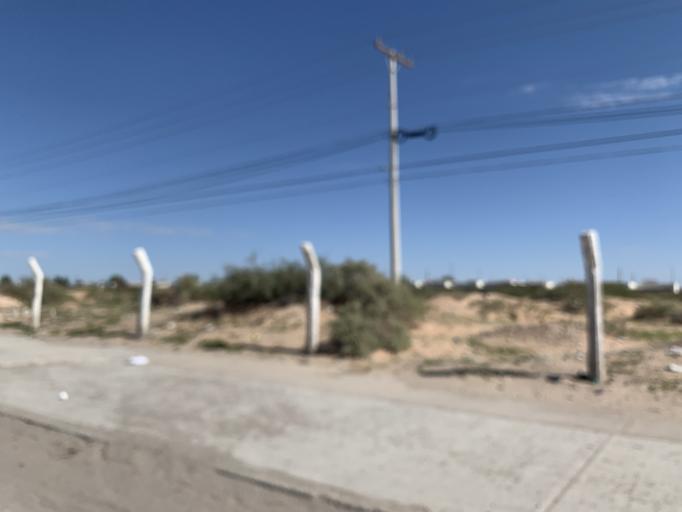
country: US
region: Texas
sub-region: El Paso County
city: San Elizario
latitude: 31.5715
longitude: -106.3500
